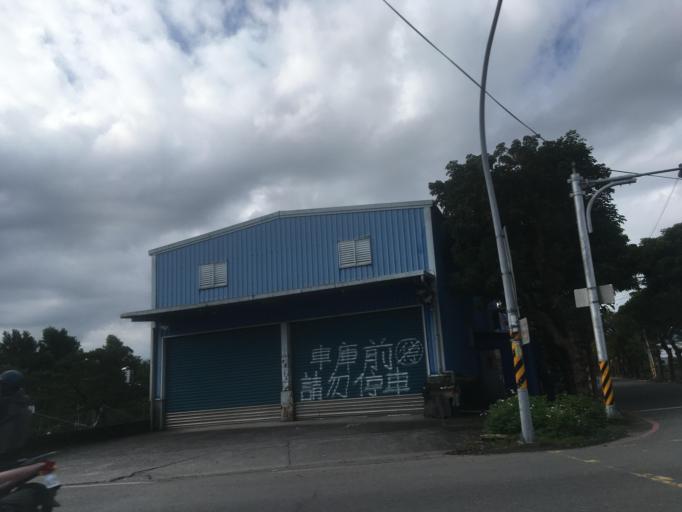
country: TW
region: Taiwan
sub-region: Yilan
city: Yilan
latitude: 24.6895
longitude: 121.7354
